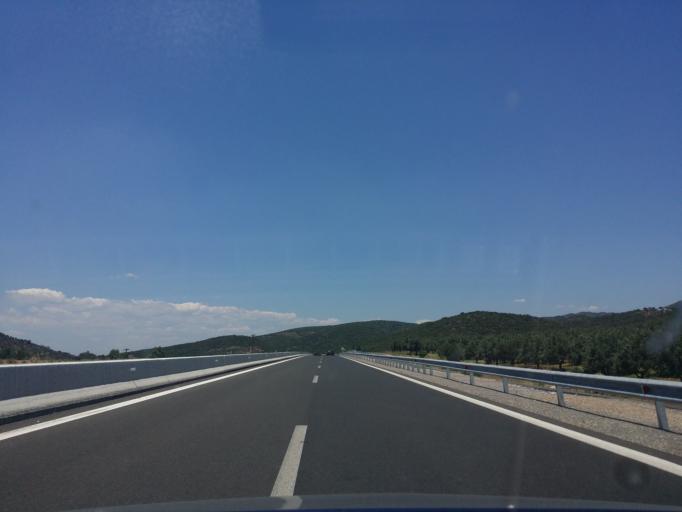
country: GR
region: Peloponnese
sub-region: Nomos Lakonias
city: Magoula
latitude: 37.1126
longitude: 22.4204
